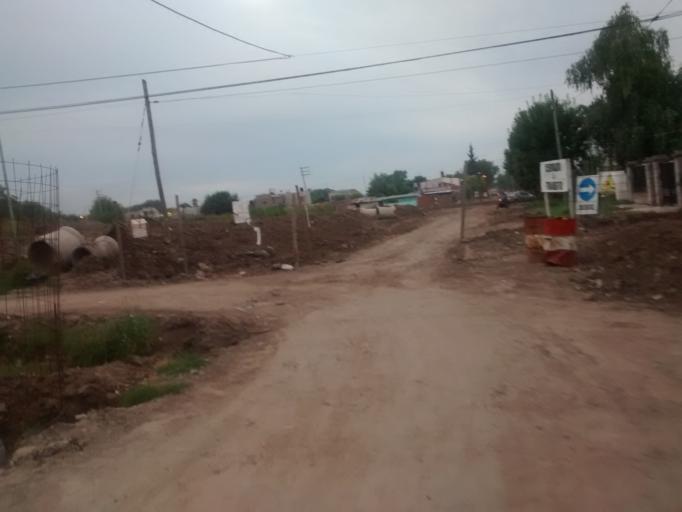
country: AR
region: Buenos Aires
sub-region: Partido de La Plata
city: La Plata
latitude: -34.9447
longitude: -57.9298
